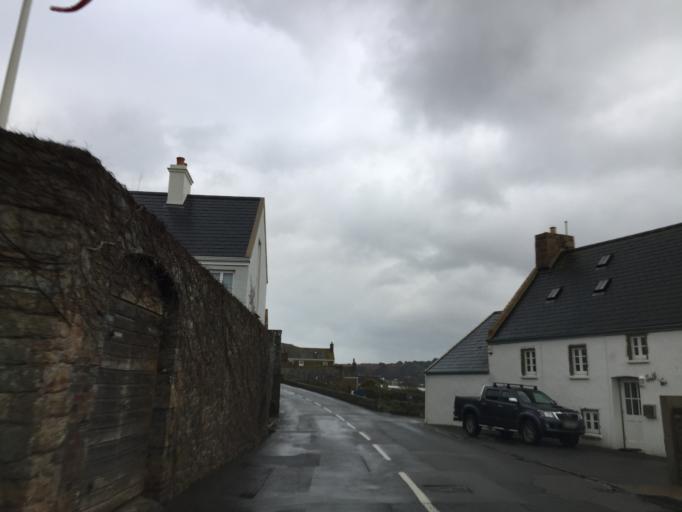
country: JE
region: St Helier
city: Saint Helier
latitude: 49.2406
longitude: -2.2440
